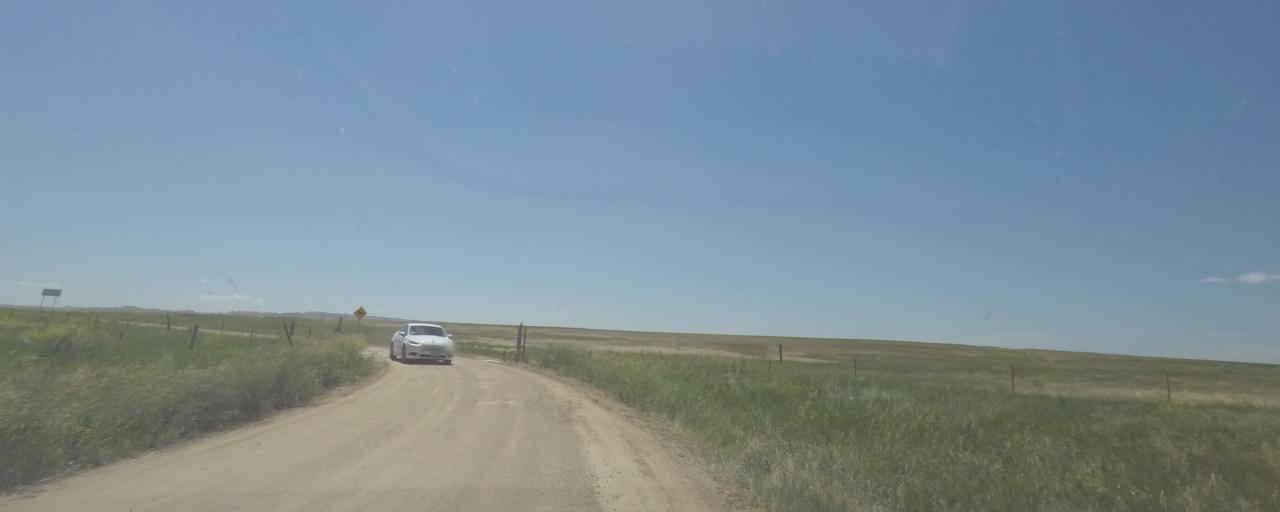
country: US
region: South Dakota
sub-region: Haakon County
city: Philip
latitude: 43.9366
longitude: -102.1583
